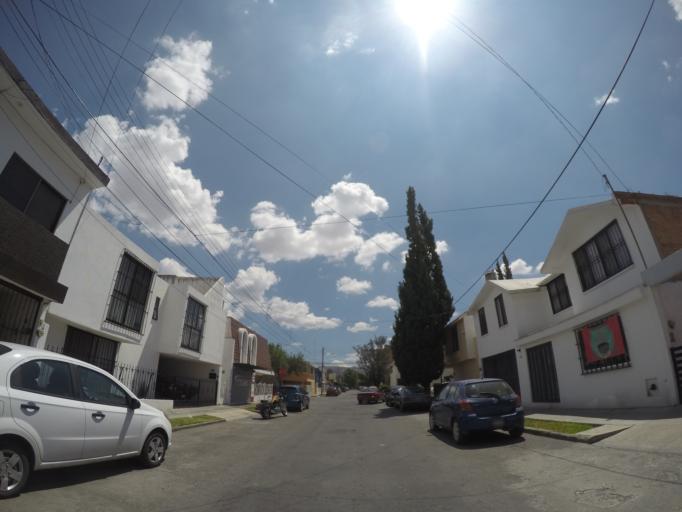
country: MX
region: San Luis Potosi
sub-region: San Luis Potosi
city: San Luis Potosi
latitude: 22.1431
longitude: -100.9922
